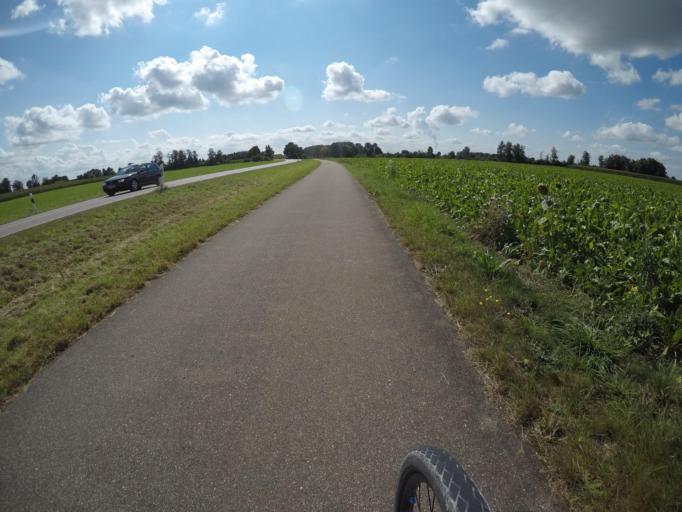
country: DE
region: Bavaria
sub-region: Swabia
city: Dillingen an der Donau
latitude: 48.6172
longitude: 10.5035
